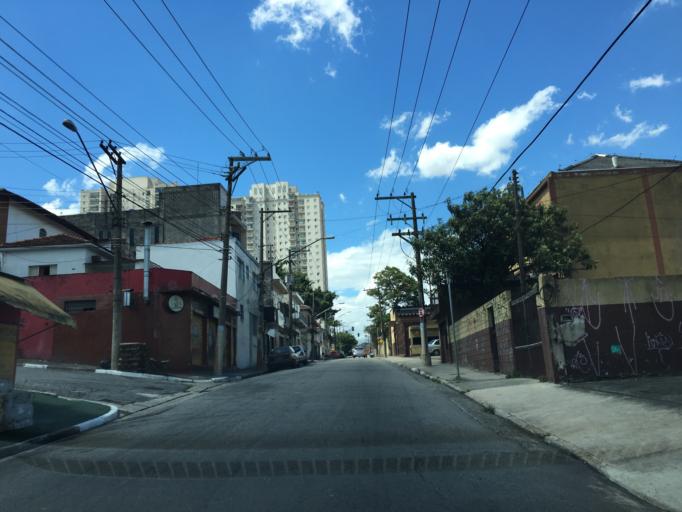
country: BR
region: Sao Paulo
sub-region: Sao Caetano Do Sul
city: Sao Caetano do Sul
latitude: -23.5801
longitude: -46.5630
